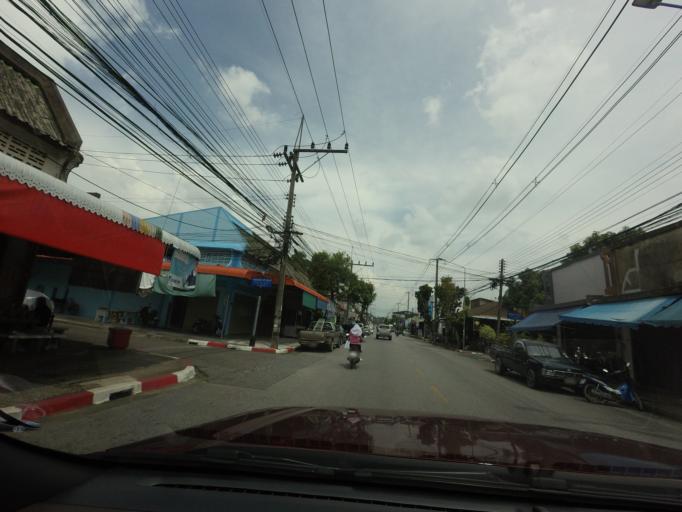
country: TH
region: Yala
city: Yala
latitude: 6.5333
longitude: 101.2857
